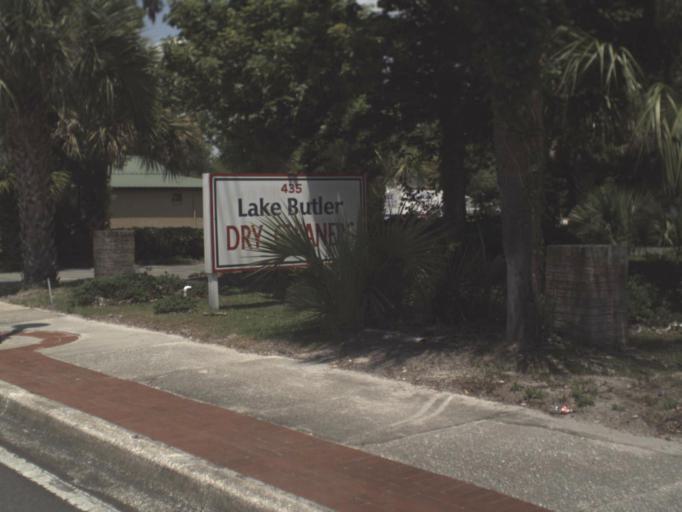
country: US
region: Florida
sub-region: Union County
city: Lake Butler
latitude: 30.0230
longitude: -82.3426
